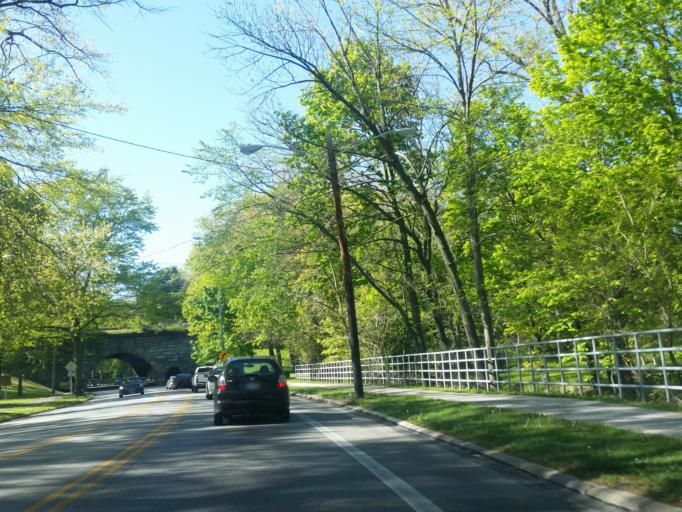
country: US
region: Ohio
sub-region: Cuyahoga County
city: Bratenahl
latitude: 41.5311
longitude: -81.6291
